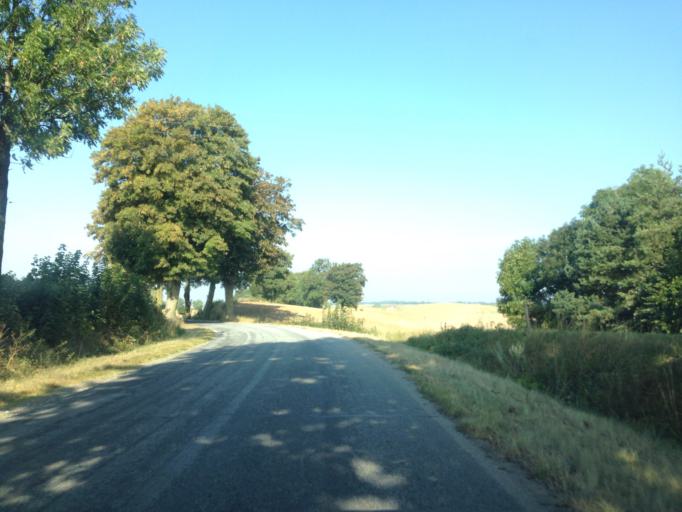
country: PL
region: Kujawsko-Pomorskie
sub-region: Powiat brodnicki
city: Brzozie
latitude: 53.2980
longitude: 19.6303
